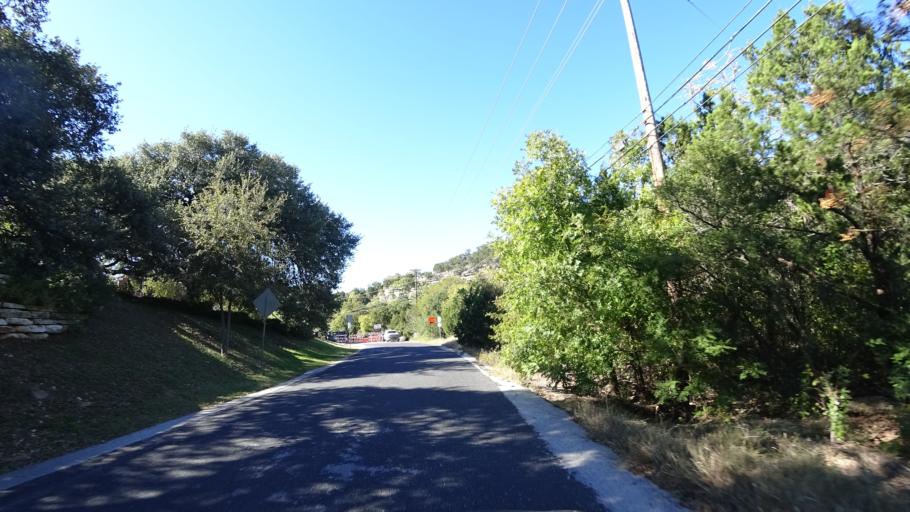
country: US
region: Texas
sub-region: Travis County
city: West Lake Hills
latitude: 30.3652
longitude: -97.7883
